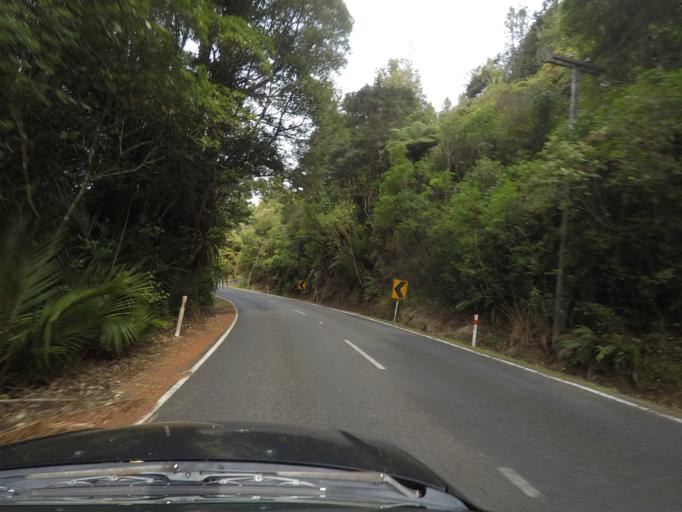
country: NZ
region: Auckland
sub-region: Auckland
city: Titirangi
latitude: -36.9420
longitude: 174.5828
